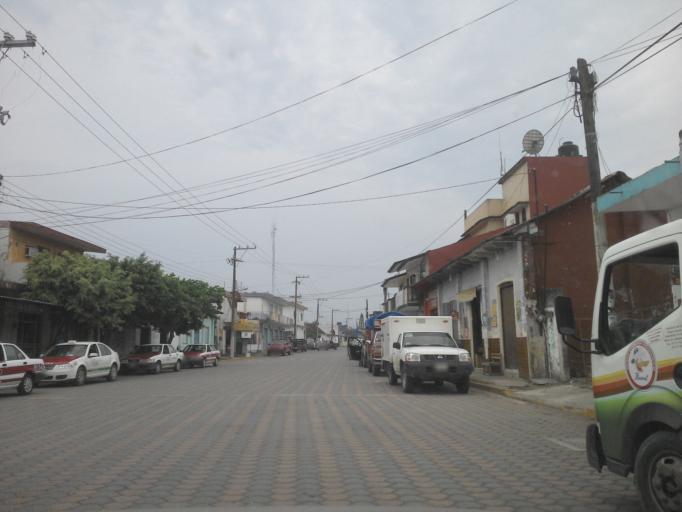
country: MX
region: Veracruz
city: Nautla
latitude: 20.2095
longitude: -96.7752
